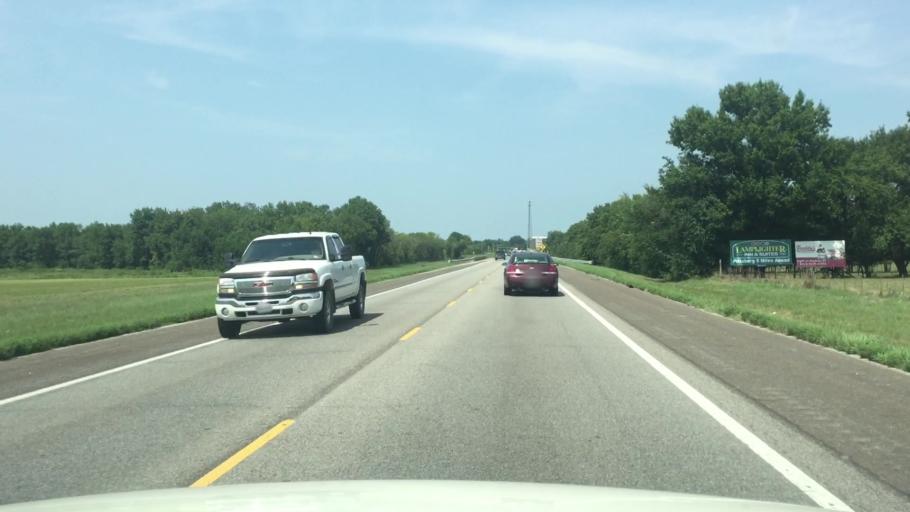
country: US
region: Kansas
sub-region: Crawford County
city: Pittsburg
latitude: 37.3722
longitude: -94.7086
